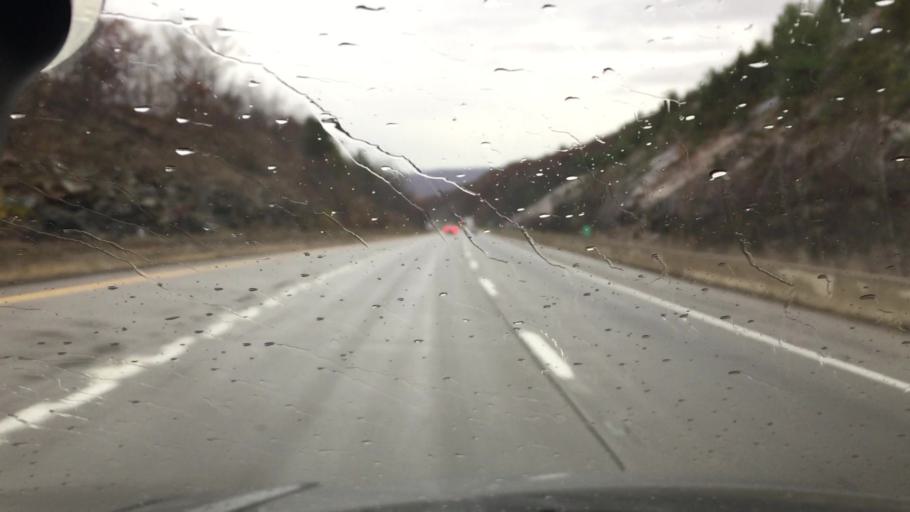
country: US
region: Pennsylvania
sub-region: Luzerne County
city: Ashley
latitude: 41.1778
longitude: -75.9405
